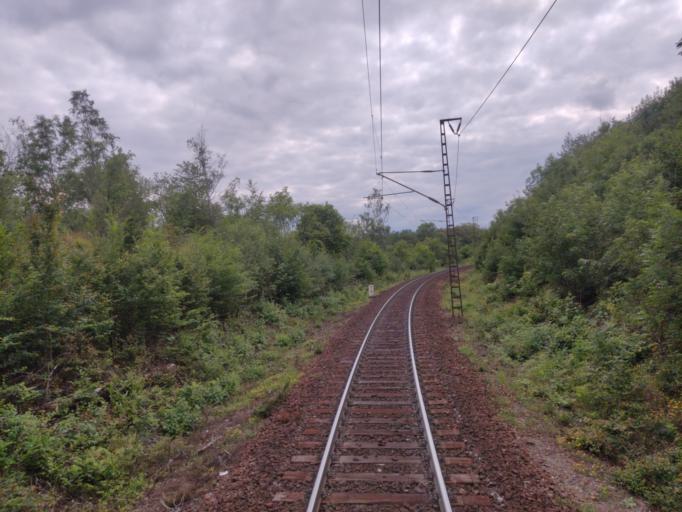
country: DE
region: Saxony-Anhalt
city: Huttenrode
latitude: 51.7841
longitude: 10.9223
